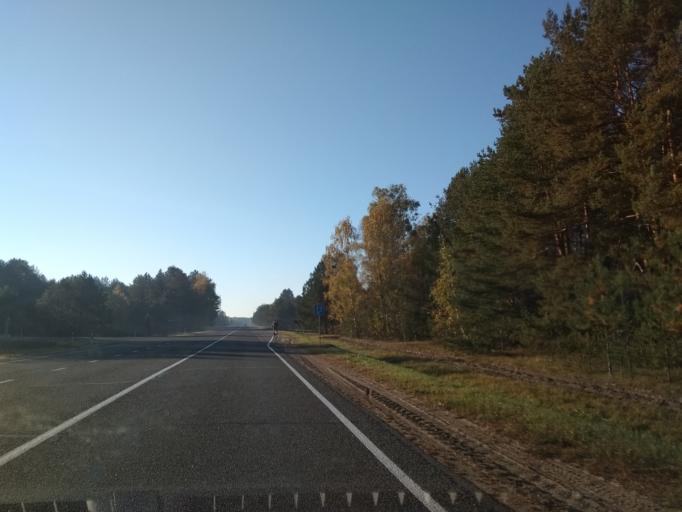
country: BY
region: Brest
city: Kobryn
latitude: 52.0763
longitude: 24.2822
